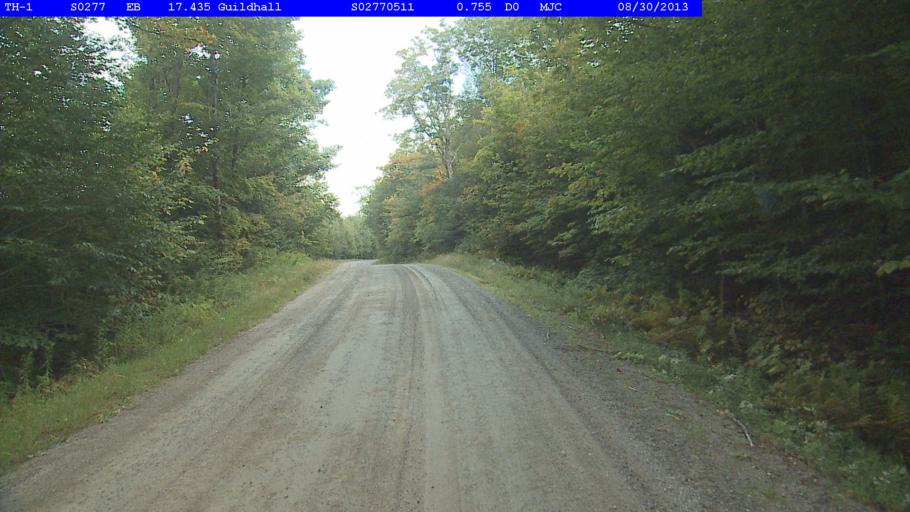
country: US
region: Vermont
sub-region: Essex County
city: Guildhall
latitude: 44.5719
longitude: -71.6550
